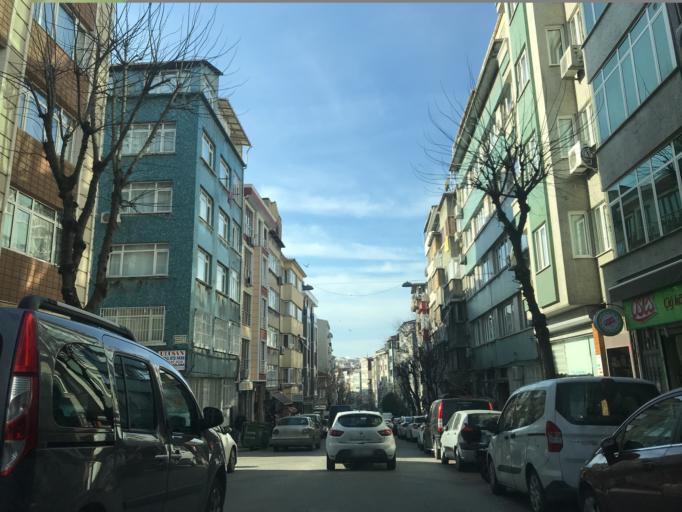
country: TR
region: Istanbul
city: Istanbul
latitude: 41.0174
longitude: 28.9467
